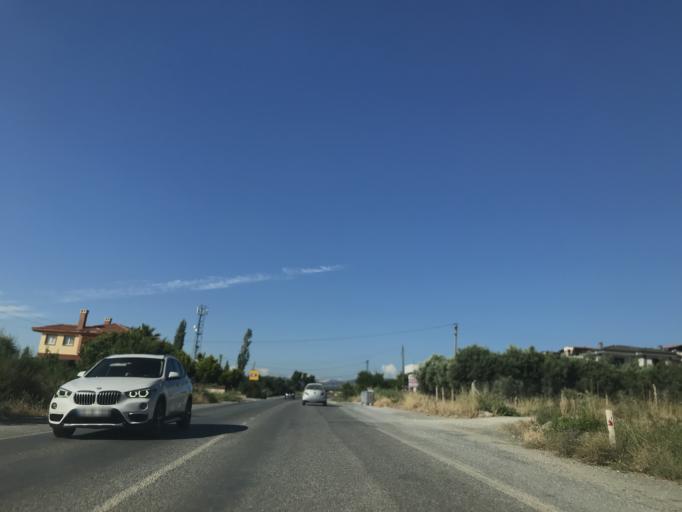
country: TR
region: Aydin
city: Davutlar
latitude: 37.7229
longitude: 27.2558
